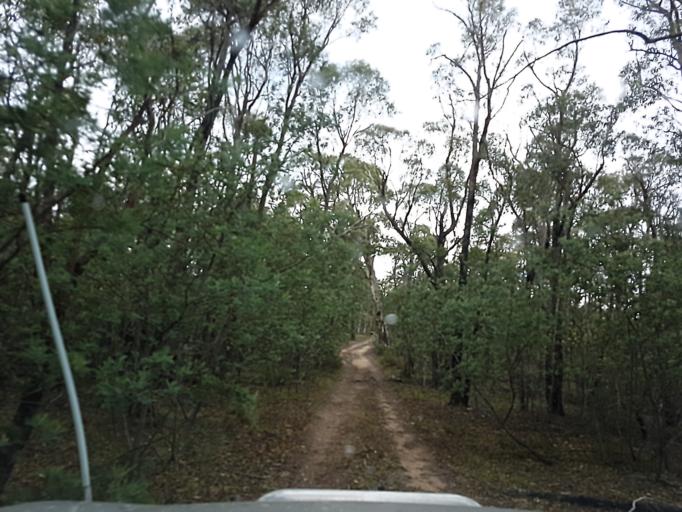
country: AU
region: New South Wales
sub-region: Snowy River
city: Jindabyne
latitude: -36.8565
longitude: 148.3325
